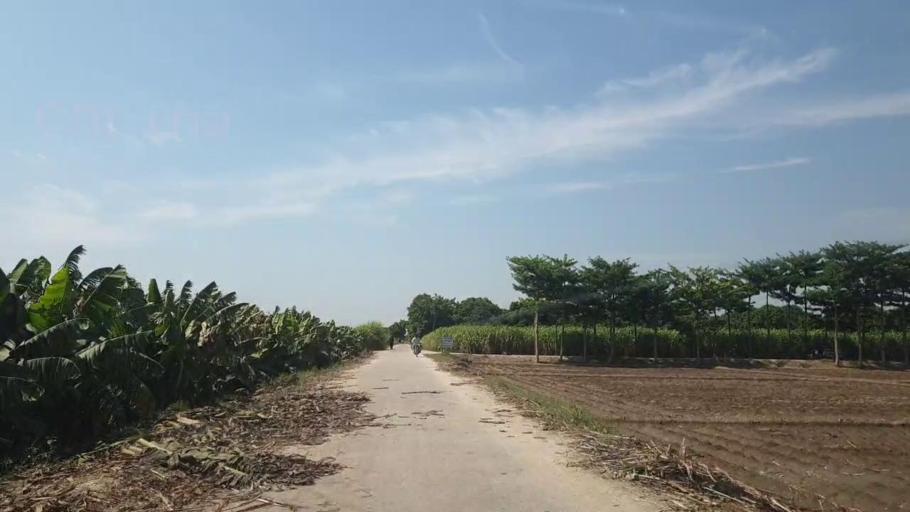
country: PK
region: Sindh
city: Tando Jam
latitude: 25.3990
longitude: 68.6287
